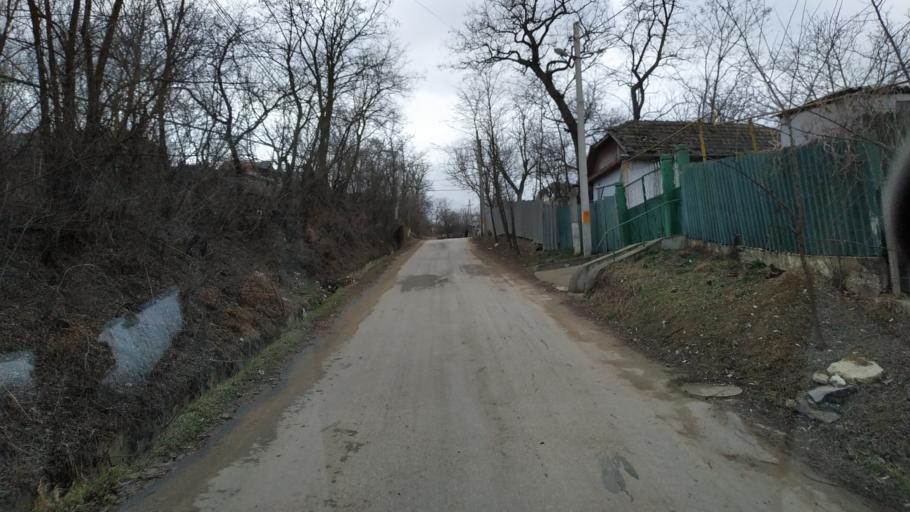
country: MD
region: Calarasi
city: Calarasi
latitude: 47.2414
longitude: 28.3106
